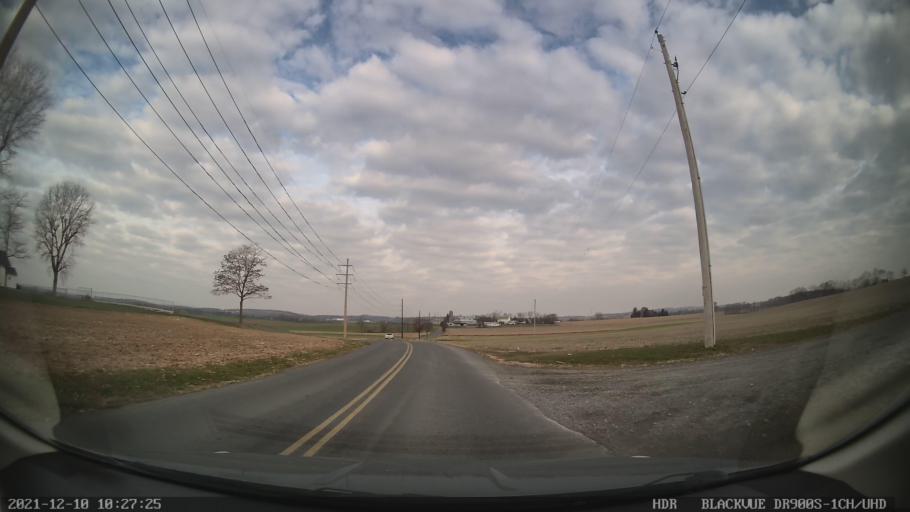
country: US
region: Pennsylvania
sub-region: Berks County
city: Kutztown
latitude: 40.5079
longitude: -75.7461
